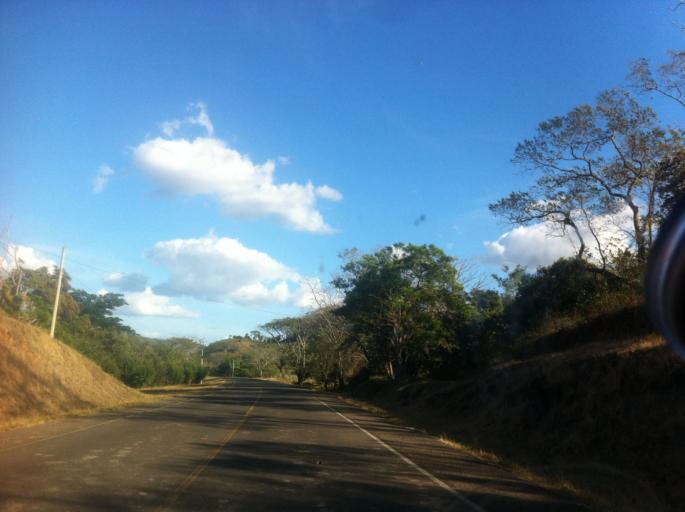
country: NI
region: Chontales
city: Acoyapa
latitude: 11.8905
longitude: -85.1093
